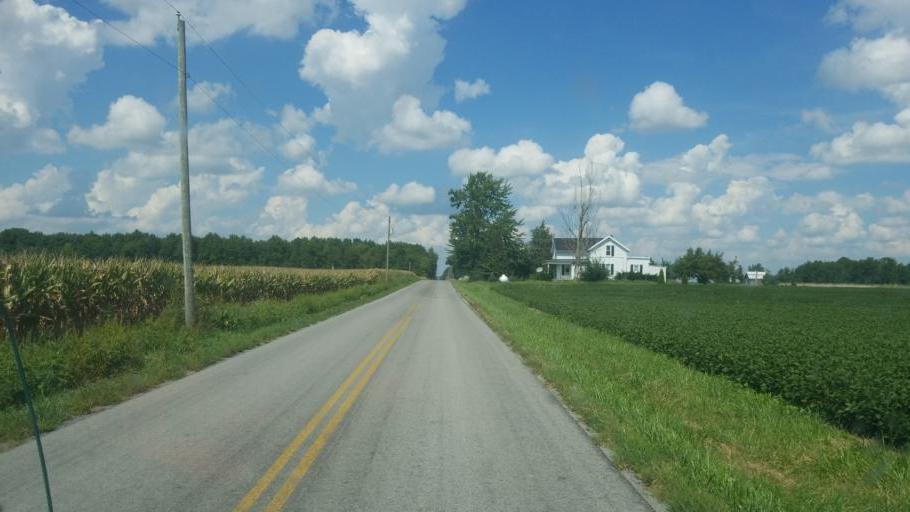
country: US
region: Ohio
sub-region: Wyandot County
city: Carey
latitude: 40.8689
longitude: -83.4191
